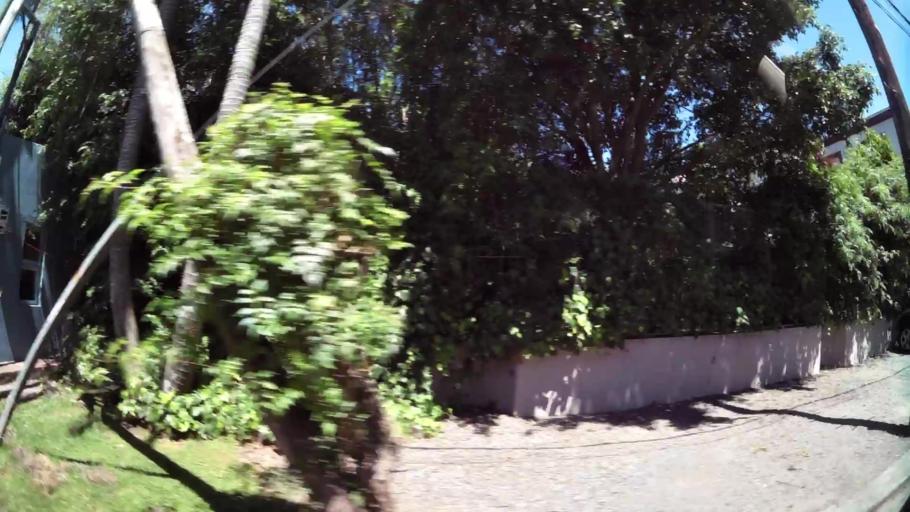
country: AR
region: Buenos Aires
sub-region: Partido de San Isidro
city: San Isidro
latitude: -34.4573
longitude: -58.5077
